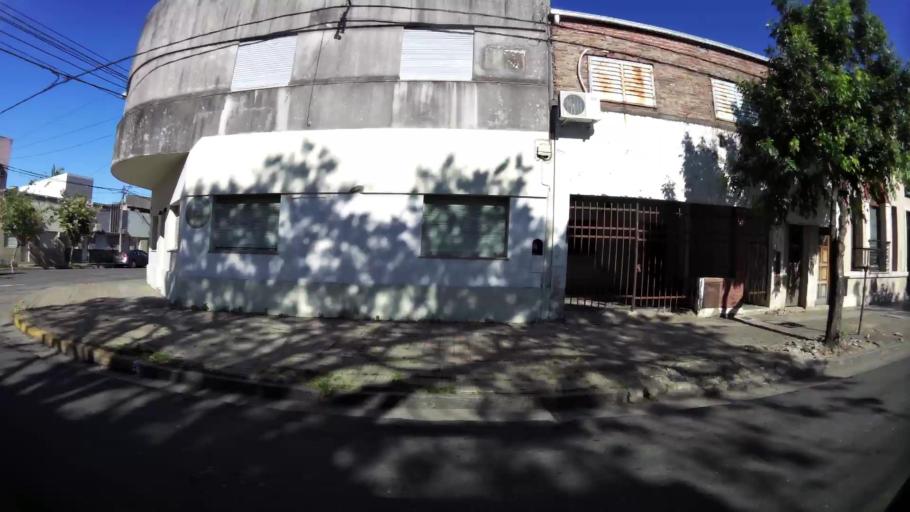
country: AR
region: Santa Fe
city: Santa Fe de la Vera Cruz
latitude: -31.6412
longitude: -60.7160
